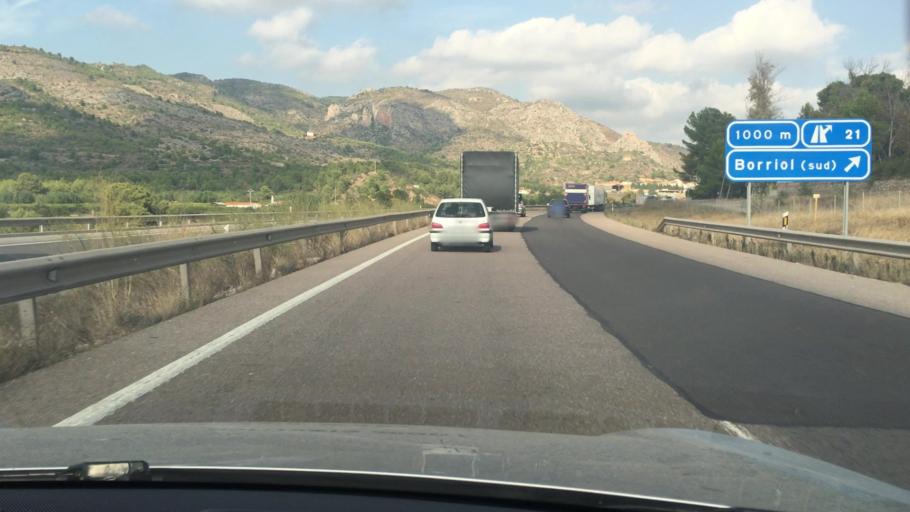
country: ES
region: Valencia
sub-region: Provincia de Castello
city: Borriol
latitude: 40.0282
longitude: -0.0873
